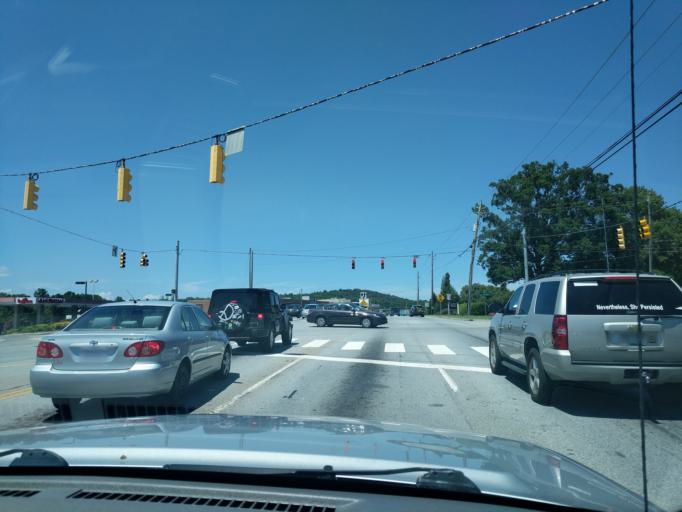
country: US
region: North Carolina
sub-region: Henderson County
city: Fletcher
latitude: 35.4420
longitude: -82.5055
